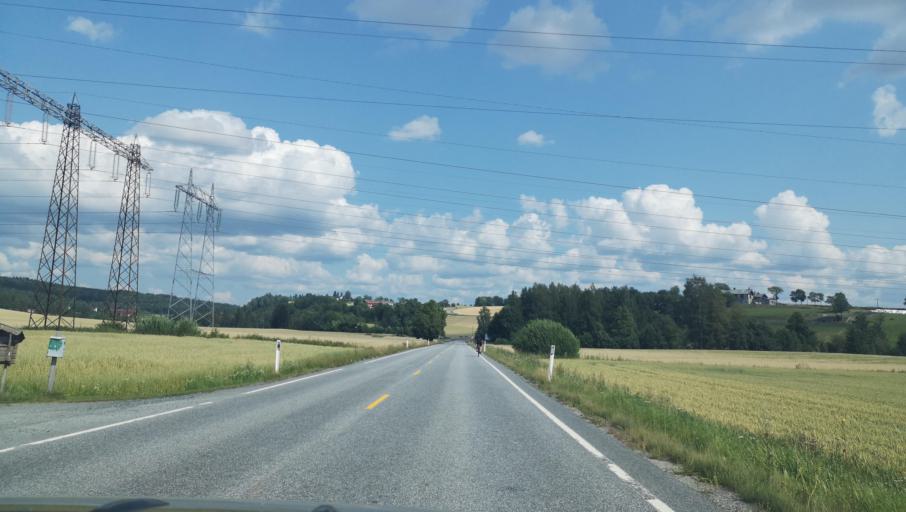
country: NO
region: Buskerud
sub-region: Ovre Eiker
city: Hokksund
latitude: 59.7230
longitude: 9.8305
